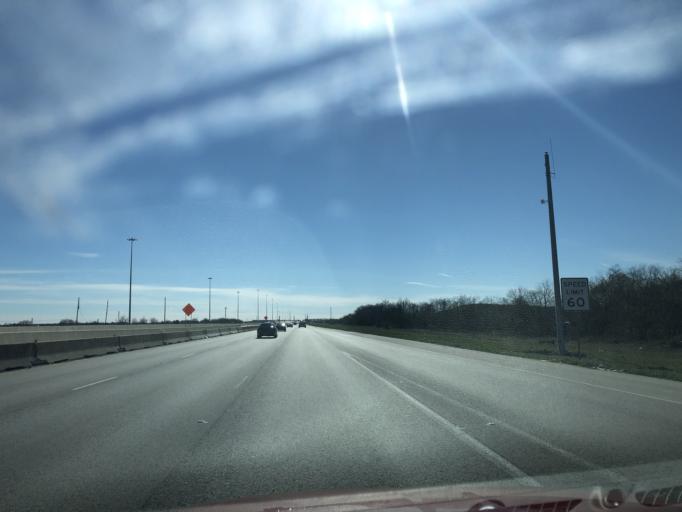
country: US
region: Texas
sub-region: Brazoria County
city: Brookside Village
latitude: 29.6385
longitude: -95.3874
